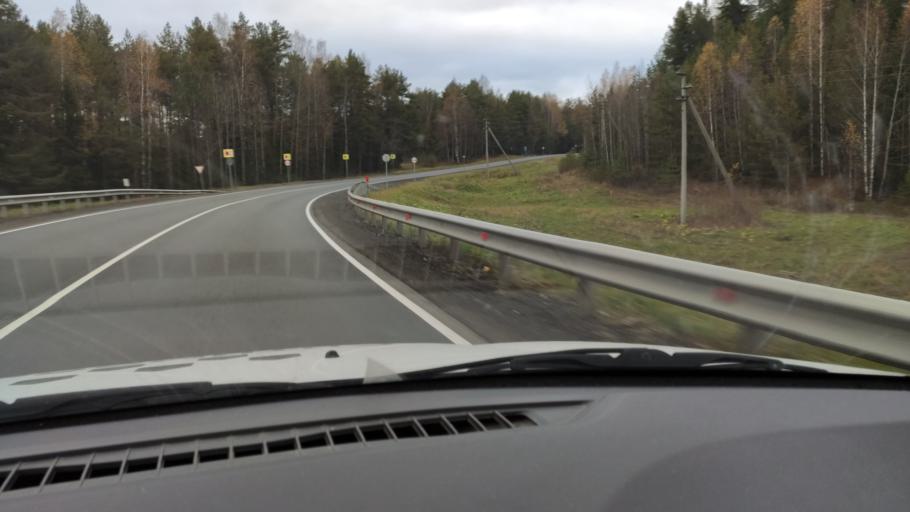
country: RU
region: Kirov
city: Belaya Kholunitsa
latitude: 58.8375
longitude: 50.6871
